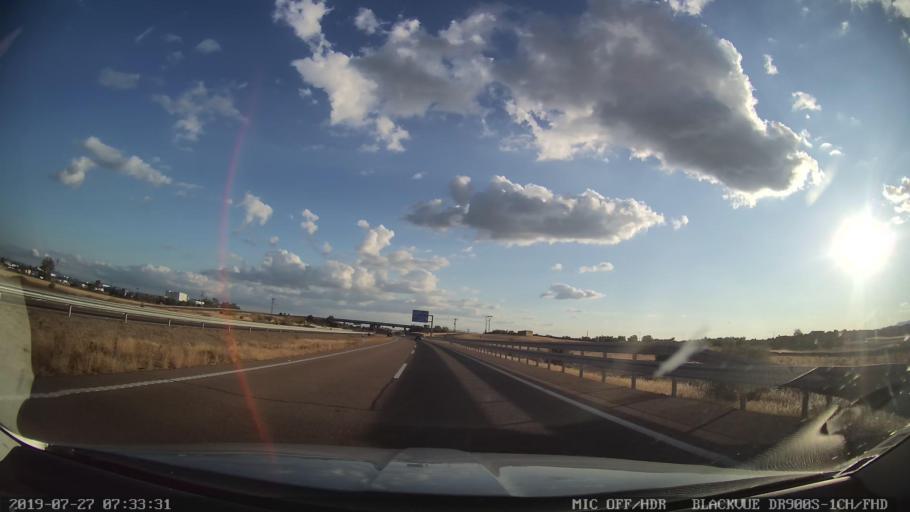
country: ES
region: Extremadura
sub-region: Provincia de Caceres
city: Miajadas
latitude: 39.1416
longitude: -5.9410
